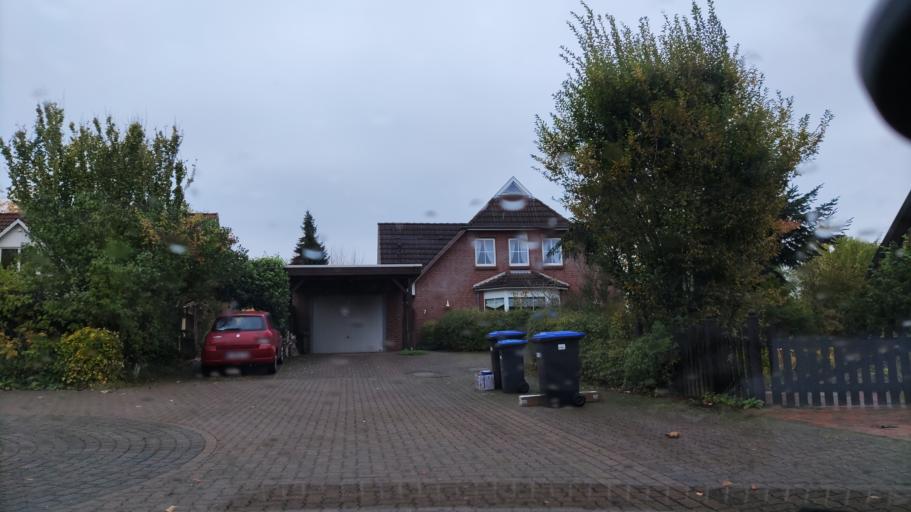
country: DE
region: Lower Saxony
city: Deutsch Evern
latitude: 53.2029
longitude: 10.4425
